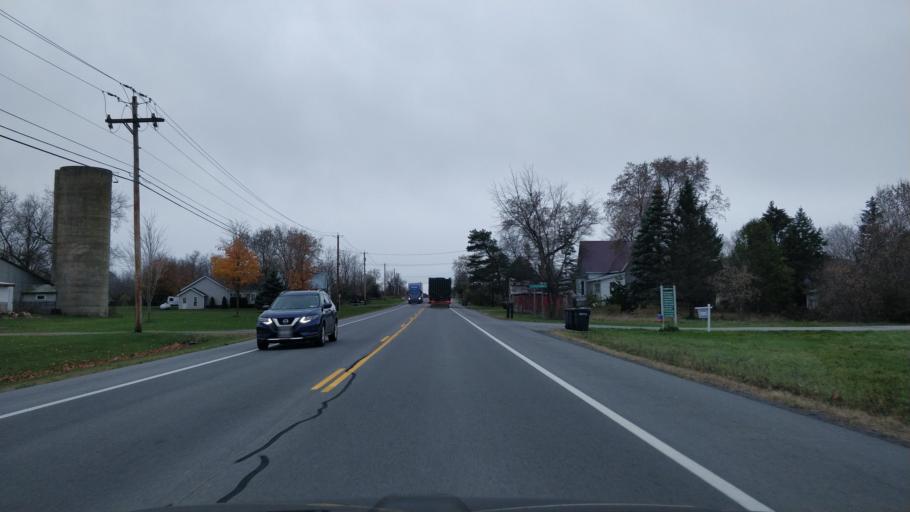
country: CA
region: Ontario
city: Brockville
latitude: 44.6249
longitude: -75.5893
